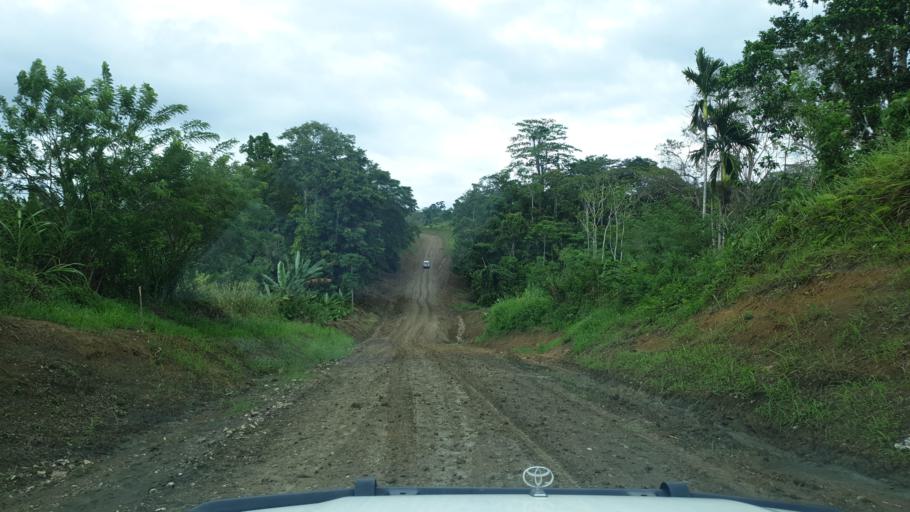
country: PG
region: Gulf
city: Kerema
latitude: -7.9865
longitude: 145.8342
